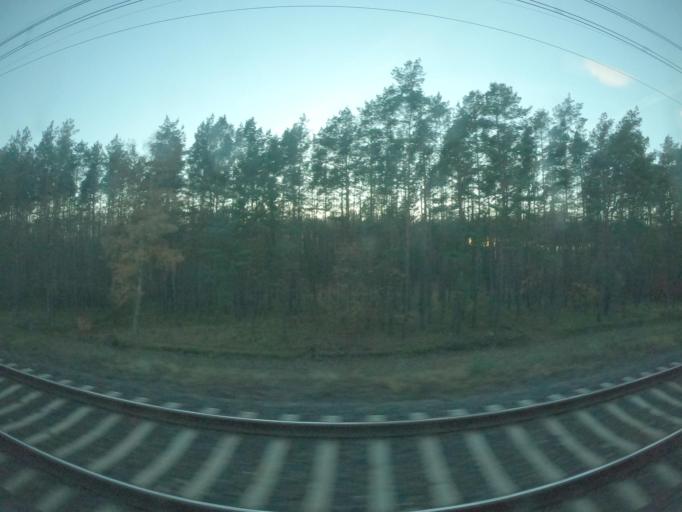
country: PL
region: West Pomeranian Voivodeship
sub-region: Powiat mysliborski
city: Boleszkowice
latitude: 52.7088
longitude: 14.5403
